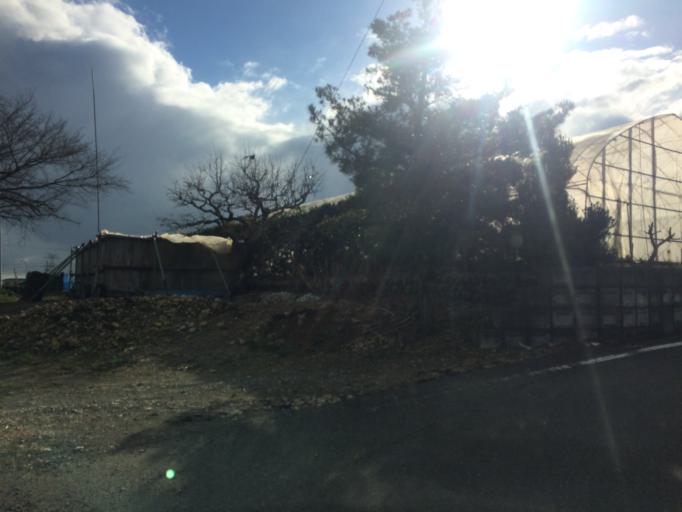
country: JP
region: Shizuoka
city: Kanaya
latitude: 34.7644
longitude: 138.1458
